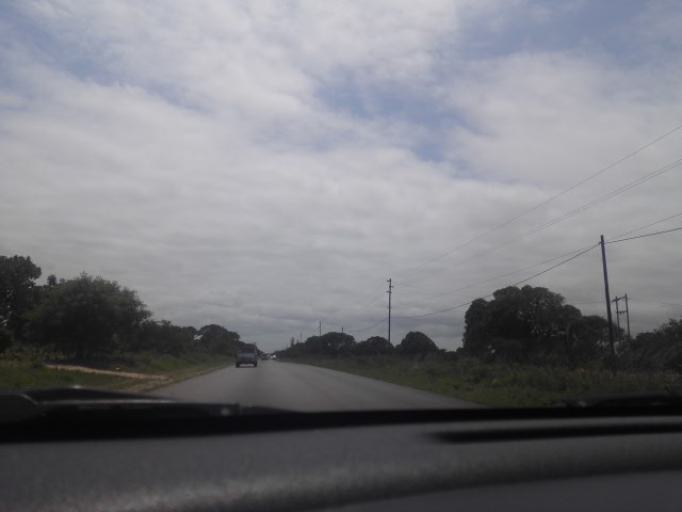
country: MZ
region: Maputo
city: Manhica
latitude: -25.4106
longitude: 32.7537
